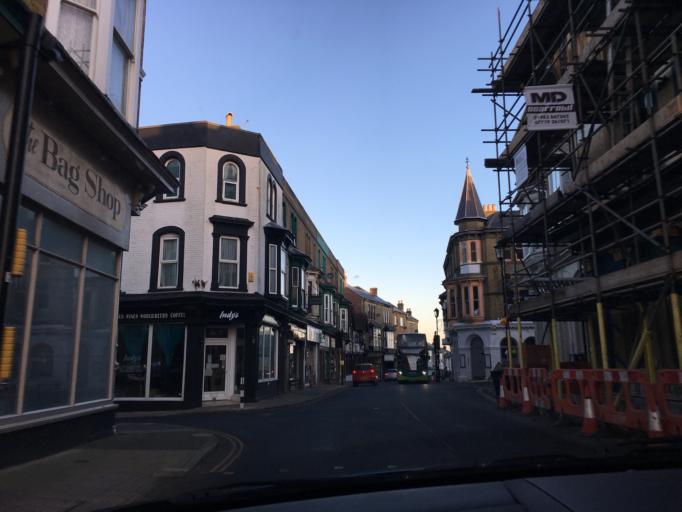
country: GB
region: England
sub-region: Isle of Wight
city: Shanklin
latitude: 50.6273
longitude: -1.1795
